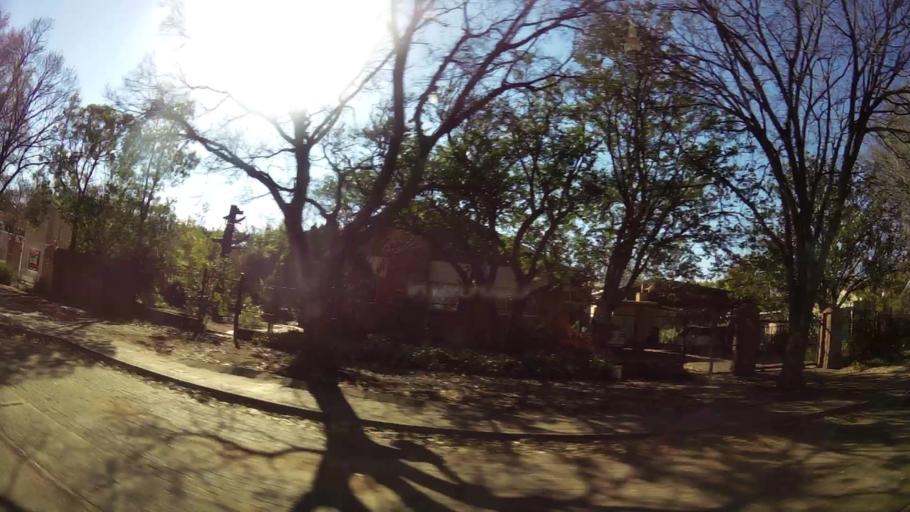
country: ZA
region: Gauteng
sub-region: City of Tshwane Metropolitan Municipality
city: Centurion
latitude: -25.8215
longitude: 28.2009
